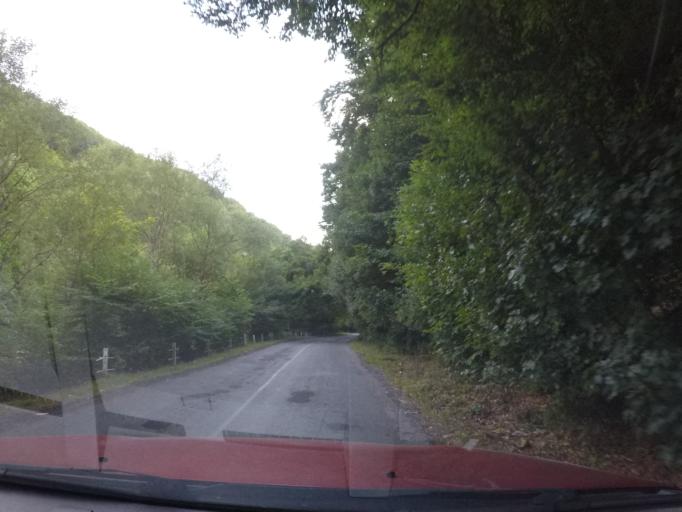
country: UA
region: Zakarpattia
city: Velykyi Bereznyi
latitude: 48.9477
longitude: 22.5003
